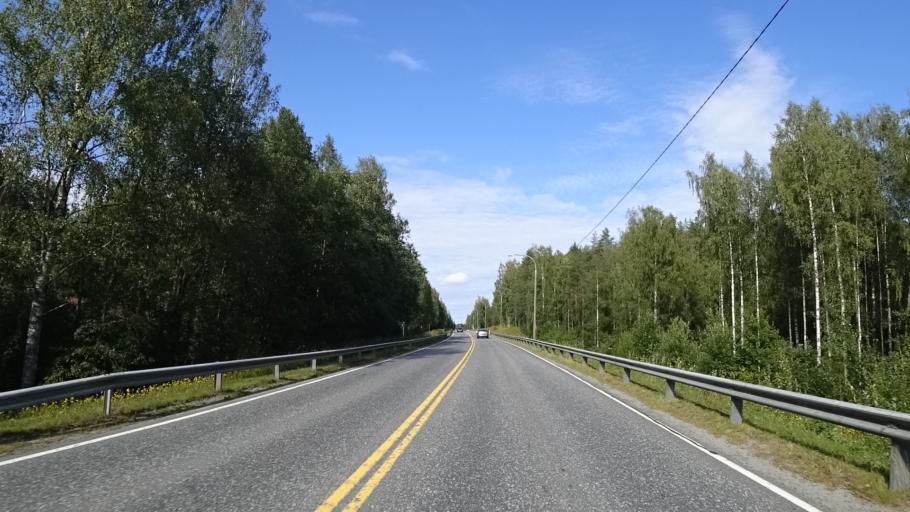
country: FI
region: North Karelia
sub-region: Joensuu
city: Eno
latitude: 62.7850
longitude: 30.0784
